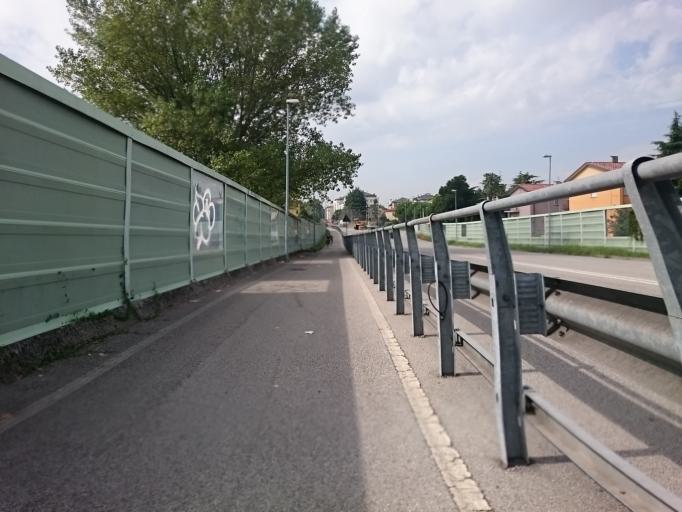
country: IT
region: Veneto
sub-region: Provincia di Padova
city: Padova
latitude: 45.4157
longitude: 11.9085
